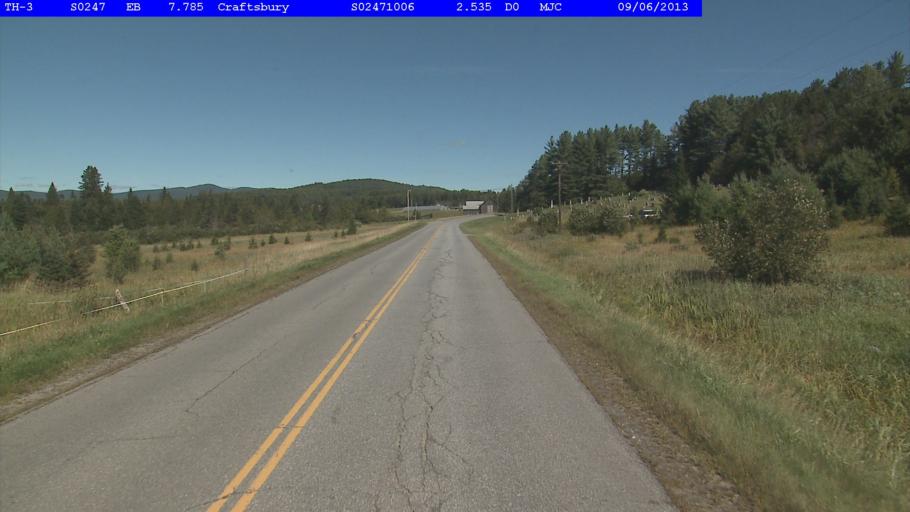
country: US
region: Vermont
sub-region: Caledonia County
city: Hardwick
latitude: 44.6478
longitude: -72.4172
